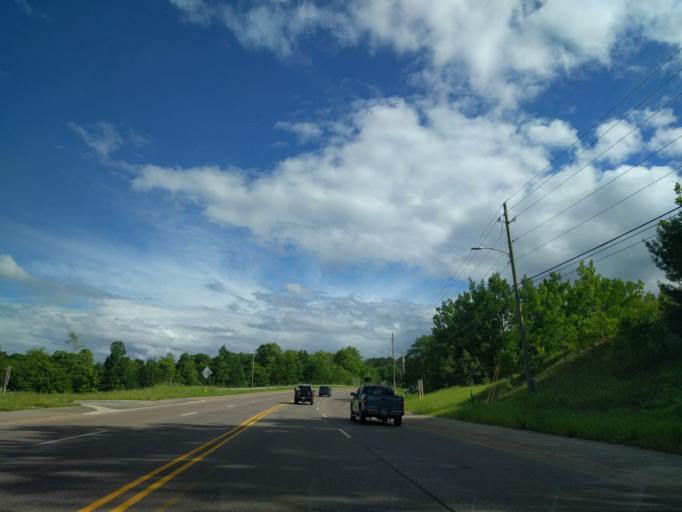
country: US
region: Michigan
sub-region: Marquette County
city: Marquette
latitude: 46.5395
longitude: -87.4180
